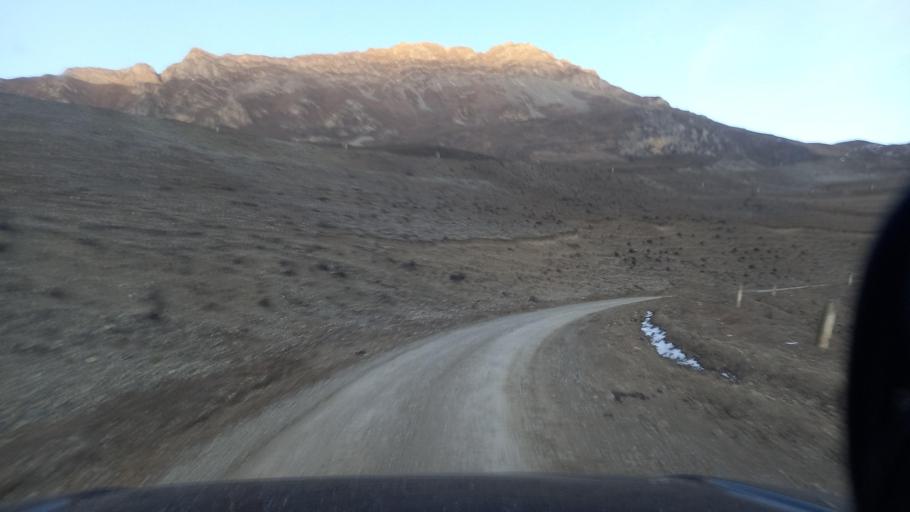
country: RU
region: Ingushetiya
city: Dzhayrakh
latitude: 42.8389
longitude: 44.5401
